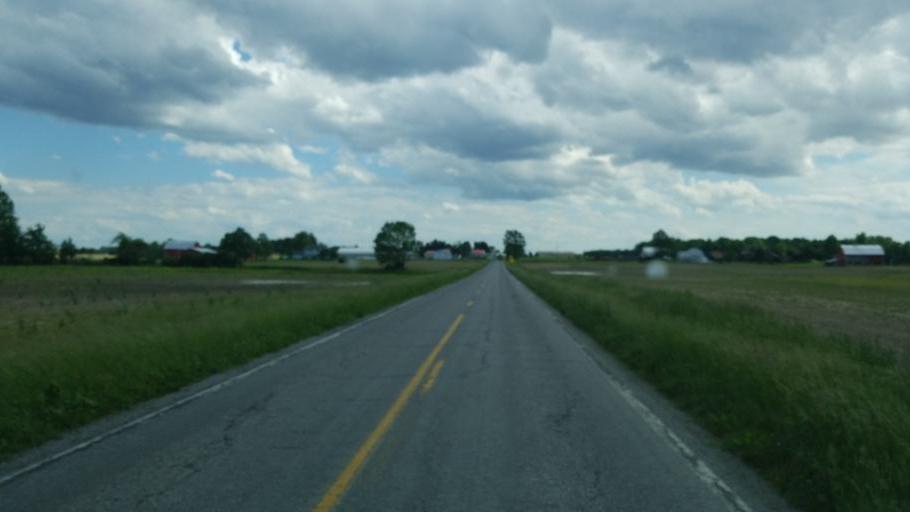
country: US
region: Ohio
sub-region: Huron County
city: Plymouth
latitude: 40.9984
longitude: -82.6062
